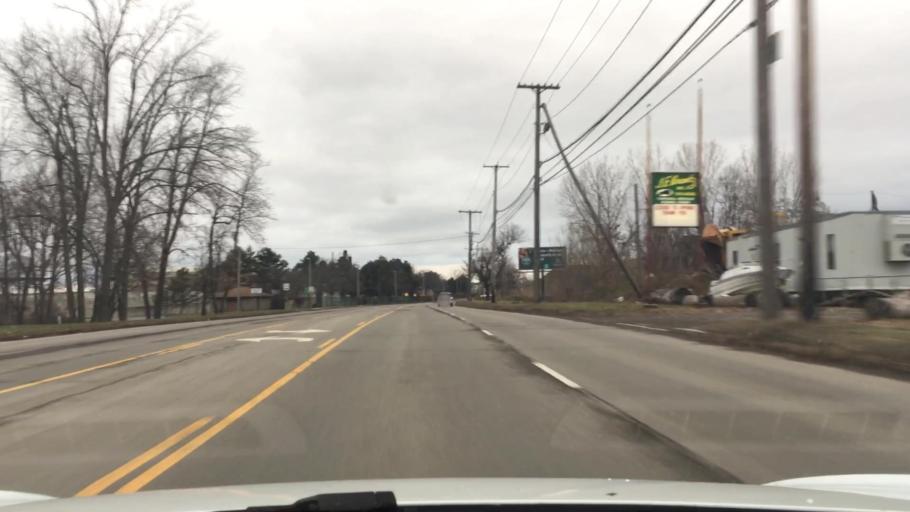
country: US
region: New York
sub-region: Erie County
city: Tonawanda
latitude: 43.0390
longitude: -78.8867
